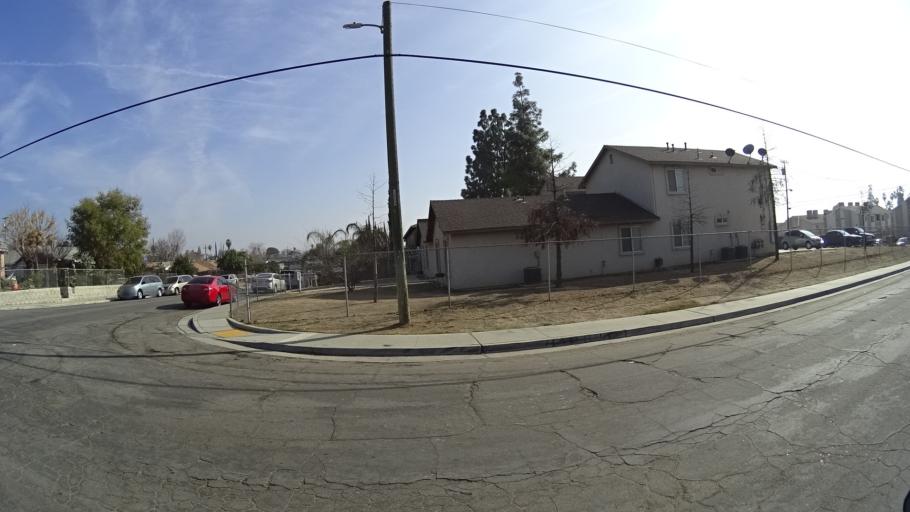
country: US
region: California
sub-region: Kern County
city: Bakersfield
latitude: 35.3850
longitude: -118.9800
